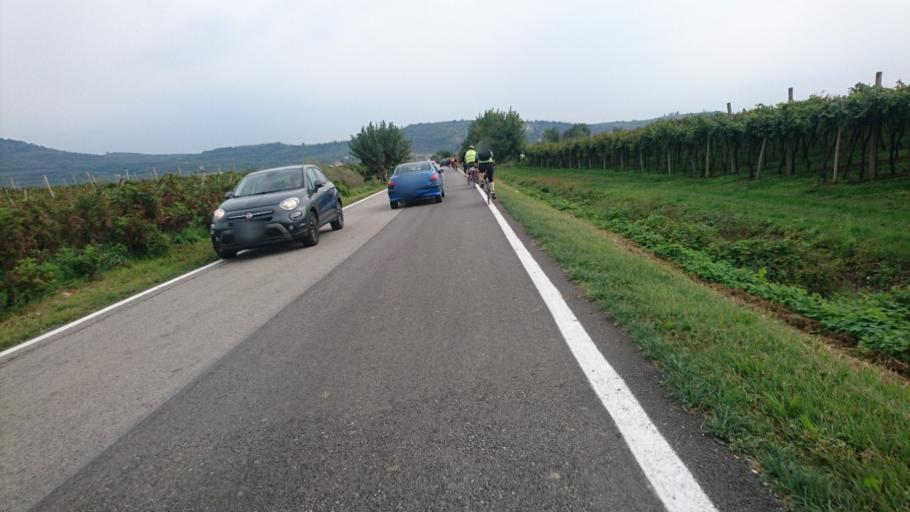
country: IT
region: Veneto
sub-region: Provincia di Verona
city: Soave
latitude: 45.4274
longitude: 11.2281
